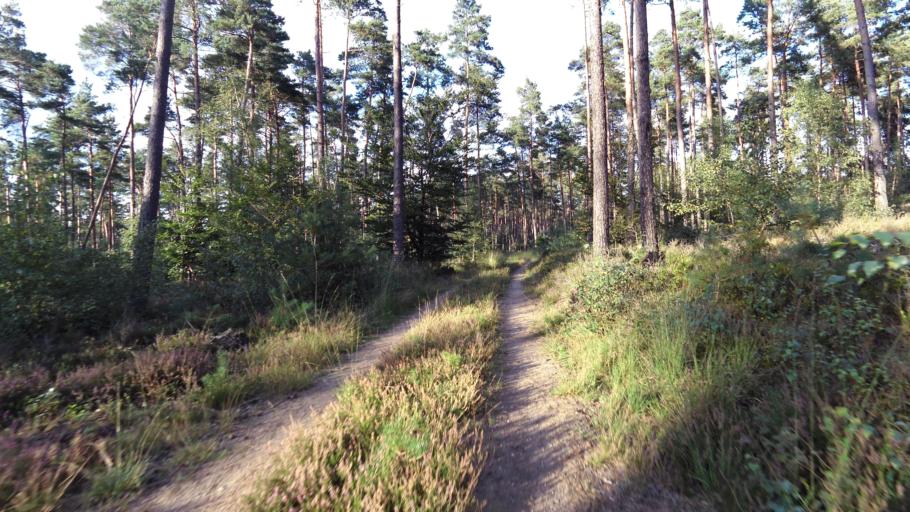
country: NL
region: Gelderland
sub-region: Gemeente Epe
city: Vaassen
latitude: 52.2774
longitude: 5.8828
